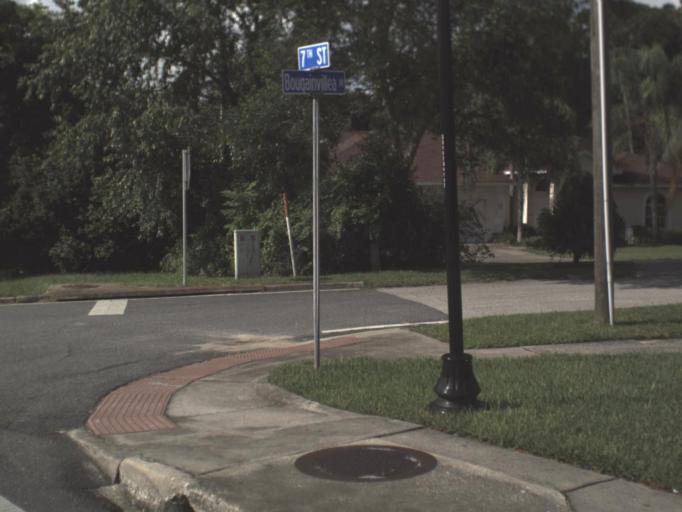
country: US
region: Florida
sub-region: Pasco County
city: Dade City
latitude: 28.3563
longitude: -82.1883
